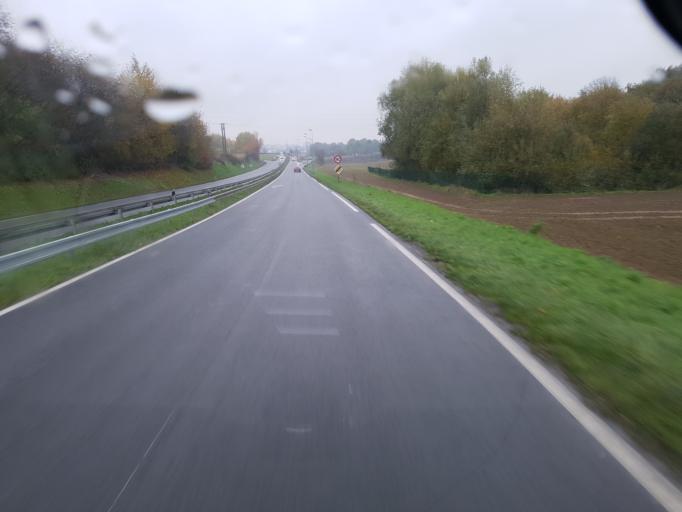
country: FR
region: Picardie
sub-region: Departement de l'Aisne
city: Harly
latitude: 49.8217
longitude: 3.2984
